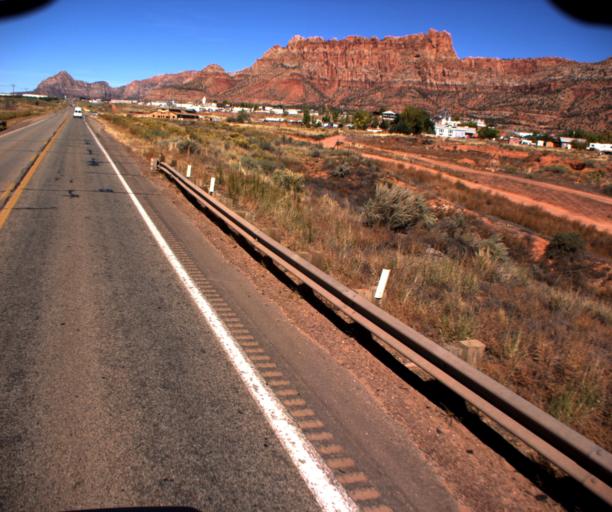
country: US
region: Arizona
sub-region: Mohave County
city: Colorado City
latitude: 36.9885
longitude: -112.9894
